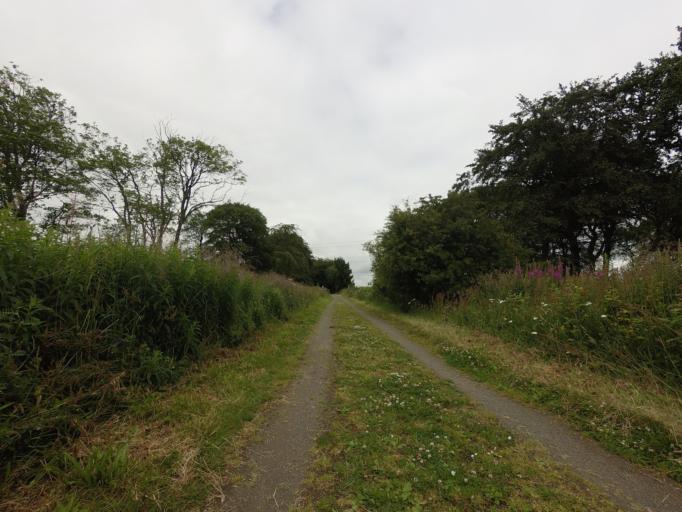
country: GB
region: Scotland
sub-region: Aberdeenshire
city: Mintlaw
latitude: 57.4908
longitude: -2.1350
